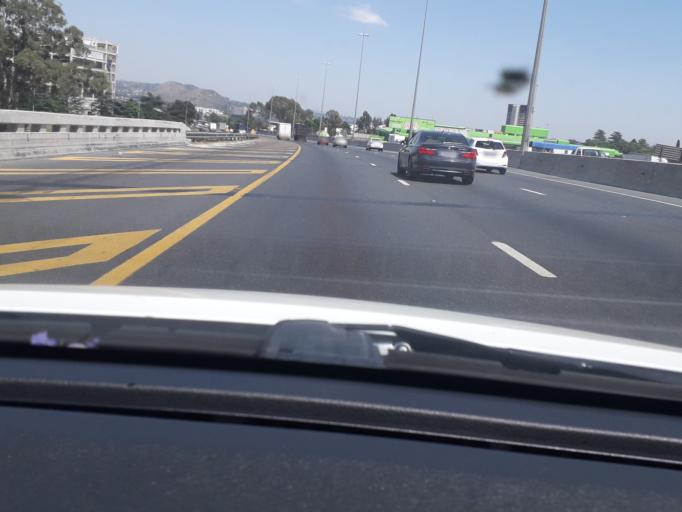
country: ZA
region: Gauteng
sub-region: Ekurhuleni Metropolitan Municipality
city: Germiston
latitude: -26.1632
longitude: 28.1675
